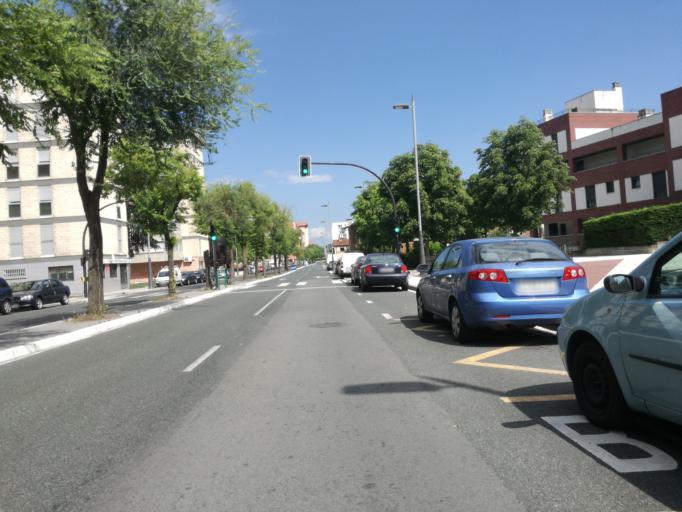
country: ES
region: Basque Country
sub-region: Provincia de Alava
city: Gasteiz / Vitoria
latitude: 42.8545
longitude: -2.7036
